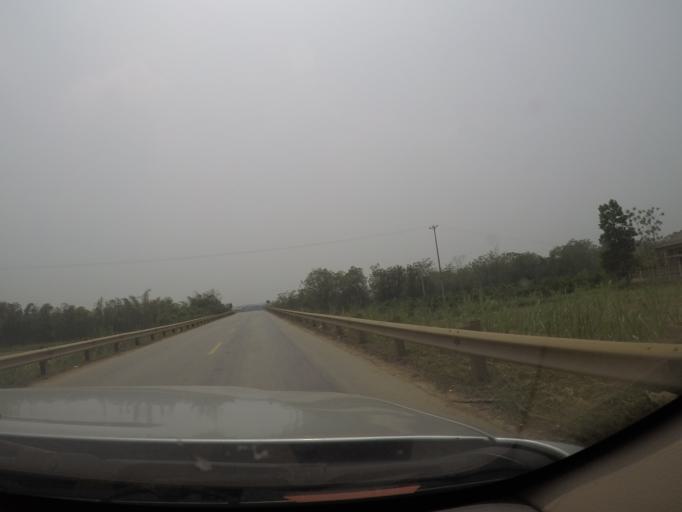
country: VN
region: Thanh Hoa
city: Thi Tran Thuong Xuan
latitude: 19.9190
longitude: 105.3948
